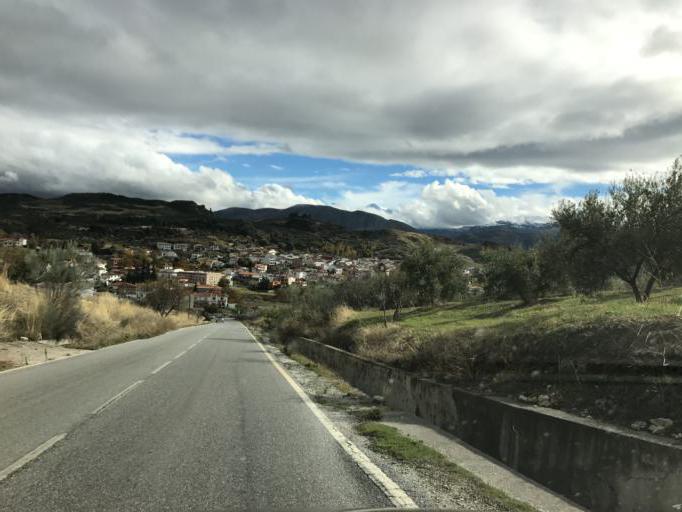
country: ES
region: Andalusia
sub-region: Provincia de Granada
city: Beas de Granada
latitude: 37.2234
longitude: -3.4867
